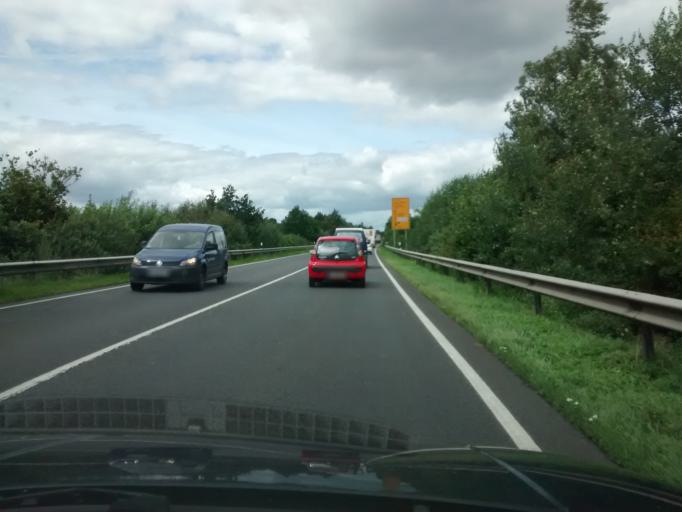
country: DE
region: Lower Saxony
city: Cappeln
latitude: 52.8241
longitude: 8.1276
